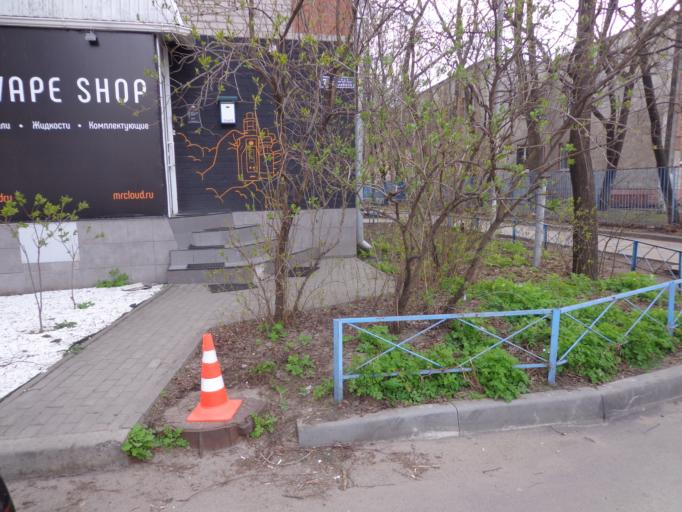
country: RU
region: Voronezj
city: Voronezh
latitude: 51.6701
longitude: 39.1925
